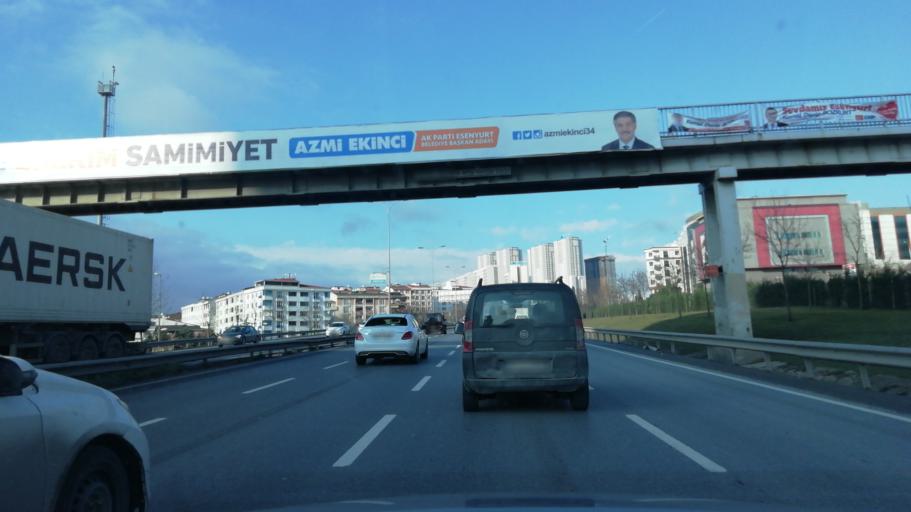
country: TR
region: Istanbul
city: Esenyurt
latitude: 41.0247
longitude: 28.6832
